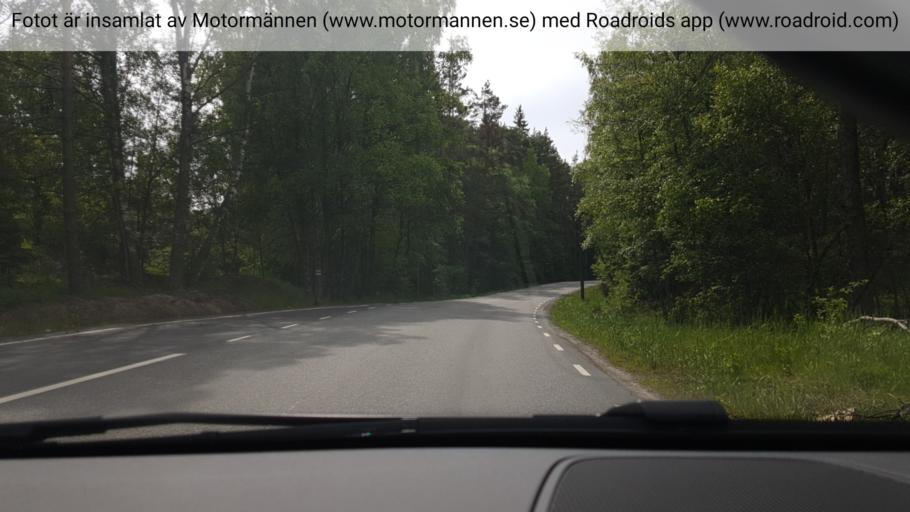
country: SE
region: Stockholm
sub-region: Haninge Kommun
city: Haninge
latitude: 59.1629
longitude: 18.1820
